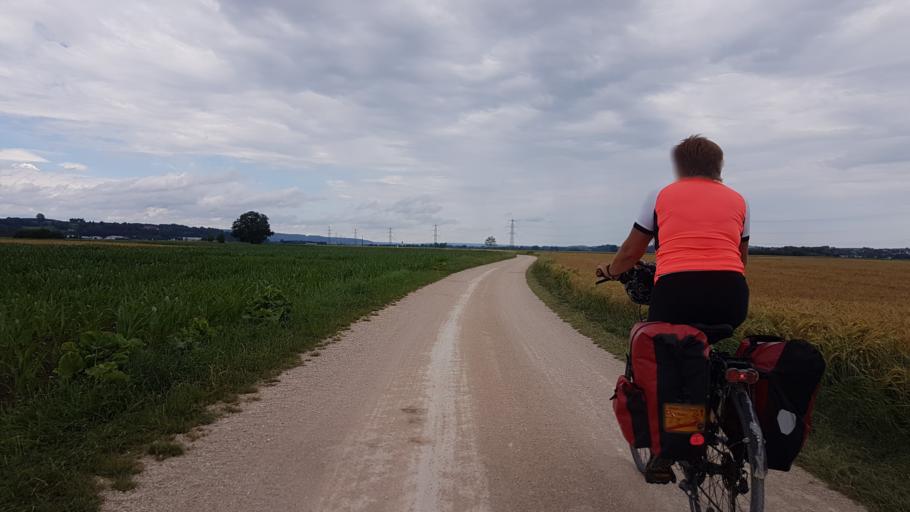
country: DE
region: Baden-Wuerttemberg
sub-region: Tuebingen Region
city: Herbertingen
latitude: 48.0875
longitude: 9.4221
